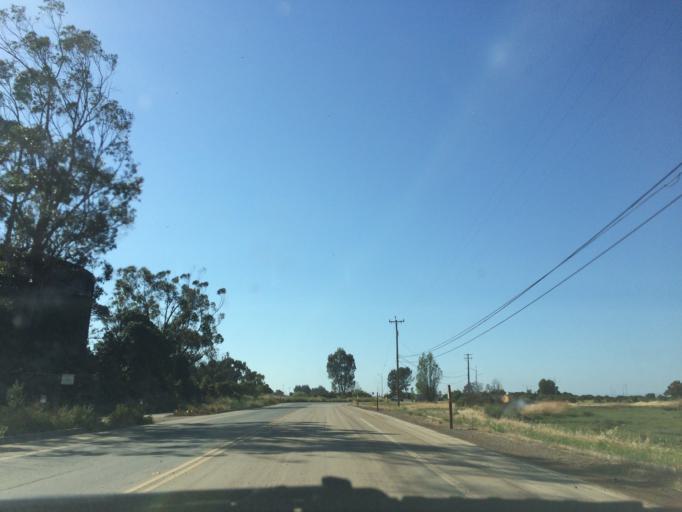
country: US
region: California
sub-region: Santa Clara County
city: Palo Alto
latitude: 37.4523
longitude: -122.1090
